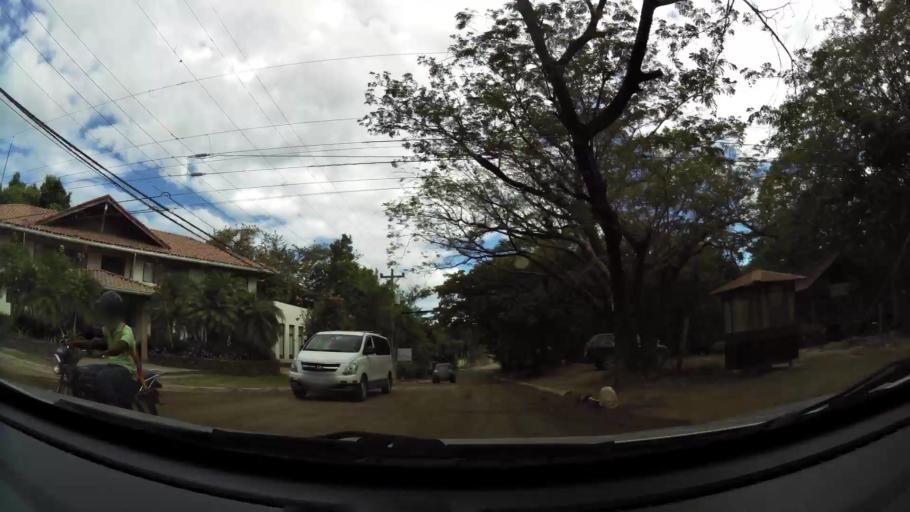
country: CR
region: Guanacaste
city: Santa Cruz
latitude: 10.2933
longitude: -85.8479
